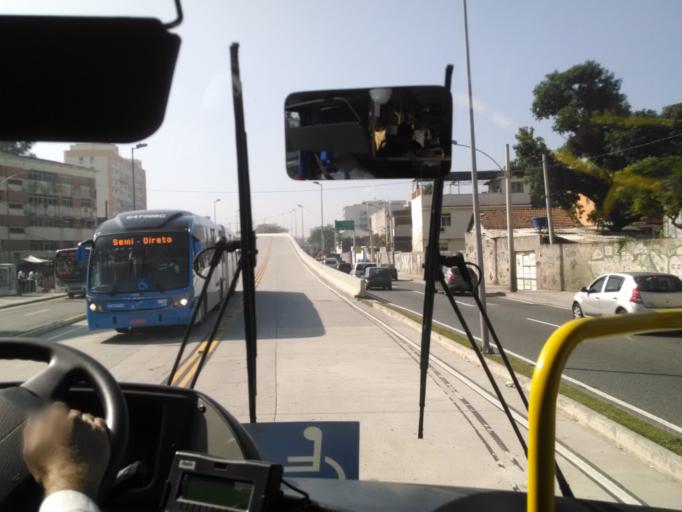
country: BR
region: Rio de Janeiro
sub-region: Sao Joao De Meriti
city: Sao Joao de Meriti
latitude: -22.8791
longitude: -43.3400
